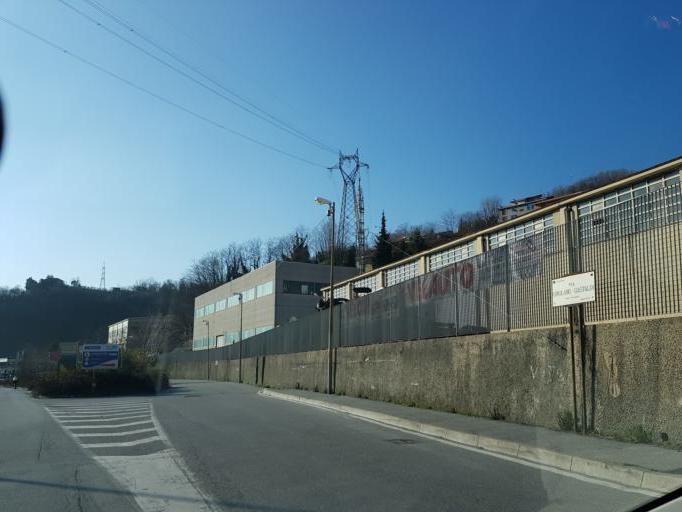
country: IT
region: Liguria
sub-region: Provincia di Genova
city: Santa Marta
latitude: 44.4880
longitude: 8.8986
